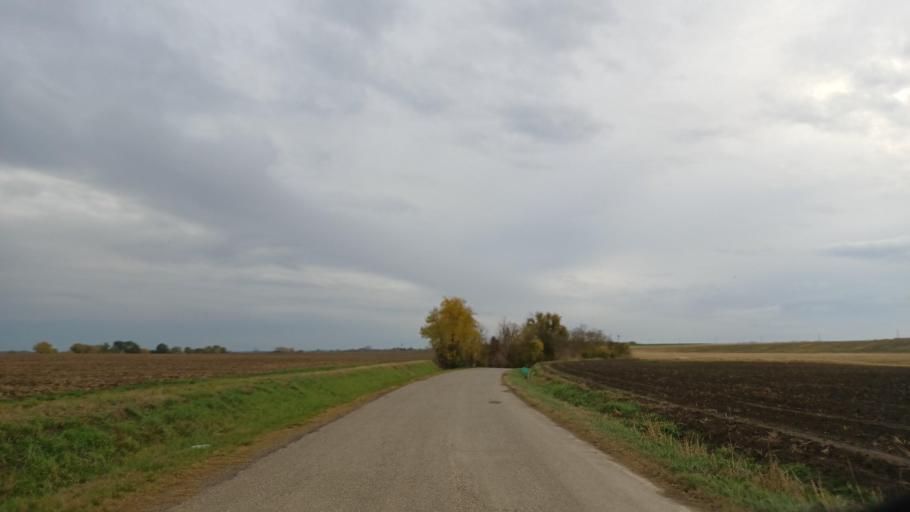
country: HU
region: Tolna
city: Nagydorog
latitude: 46.6497
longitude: 18.6086
